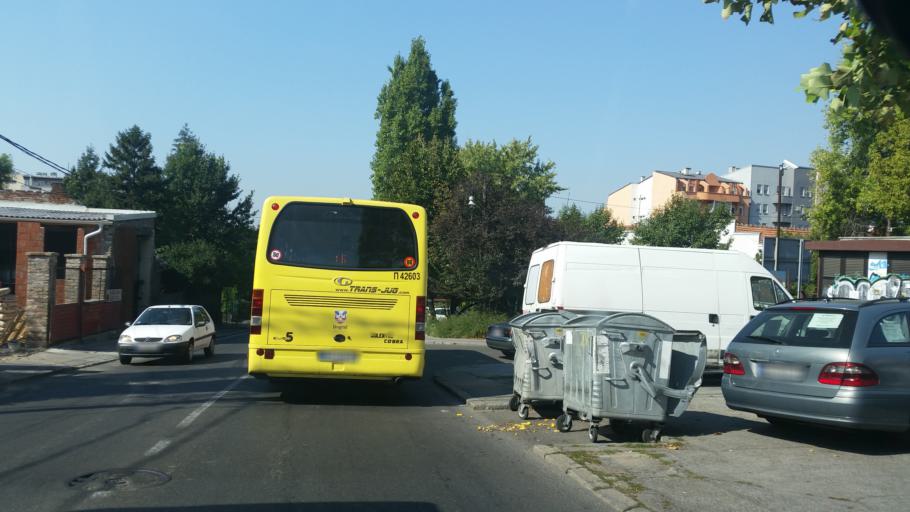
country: RS
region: Central Serbia
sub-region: Belgrade
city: Vracar
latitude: 44.7918
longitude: 20.5001
